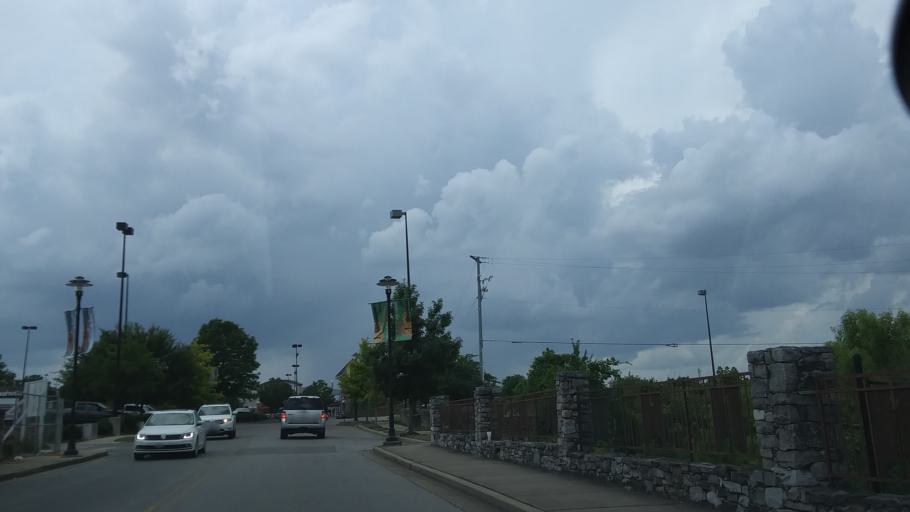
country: US
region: Tennessee
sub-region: Davidson County
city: Belle Meade
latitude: 36.1365
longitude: -86.8856
